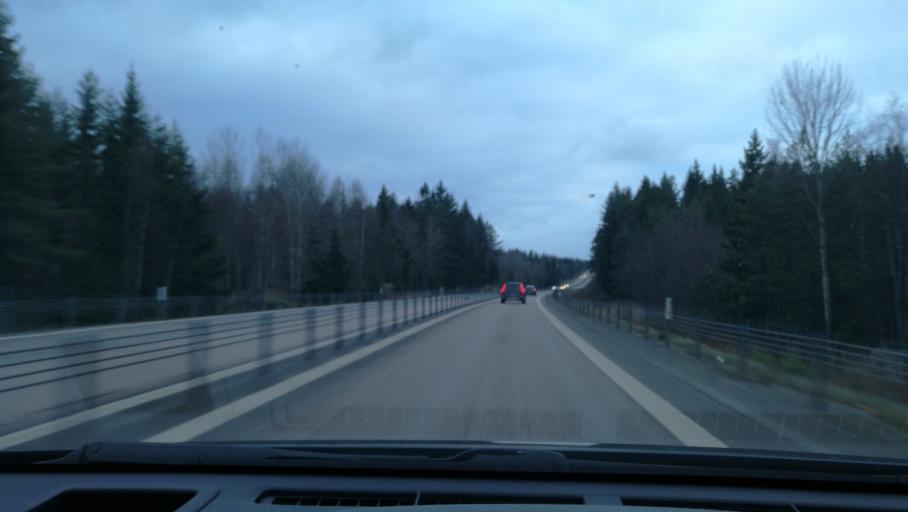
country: SE
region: Soedermanland
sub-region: Eskilstuna Kommun
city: Kvicksund
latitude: 59.4036
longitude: 16.3340
